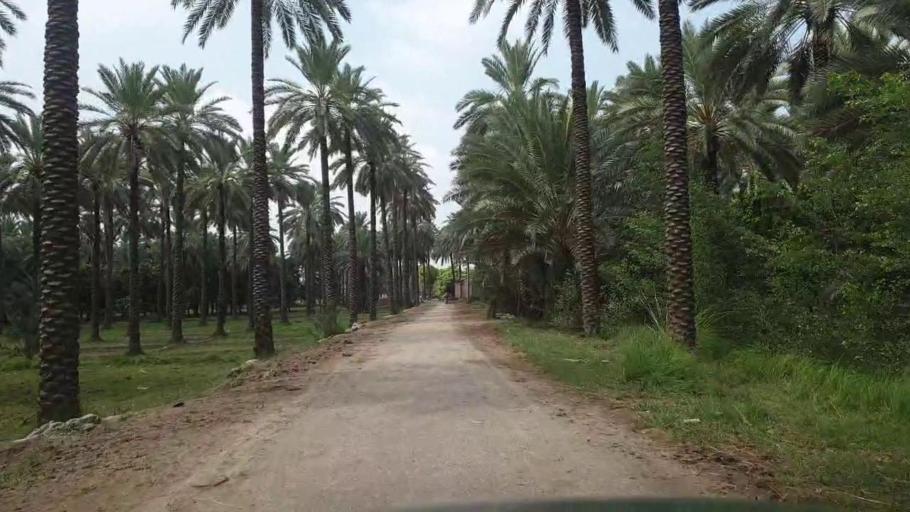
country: PK
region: Sindh
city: Pir jo Goth
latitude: 27.6146
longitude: 68.6754
